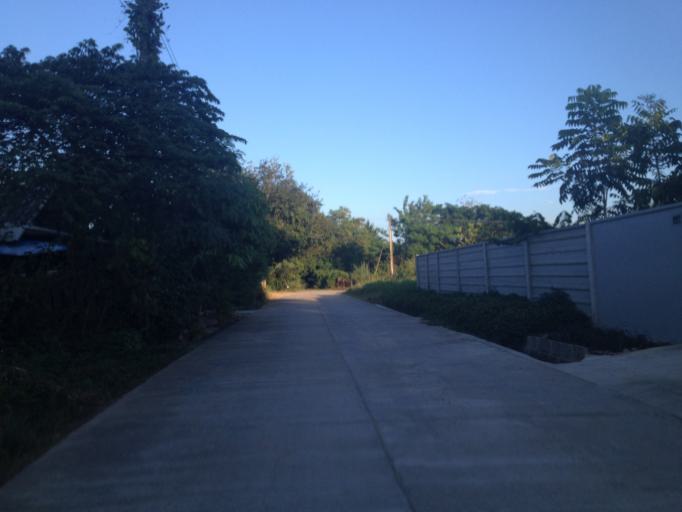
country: TH
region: Chiang Mai
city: Hang Dong
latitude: 18.6796
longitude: 98.9064
